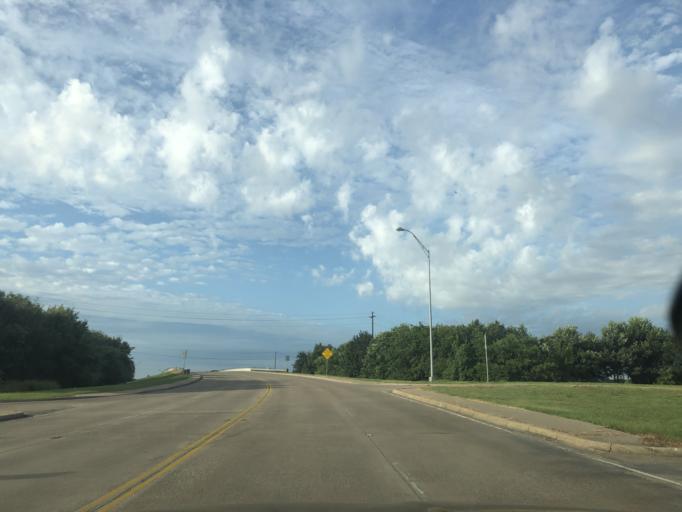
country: US
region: Texas
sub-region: Dallas County
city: Sunnyvale
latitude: 32.8473
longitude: -96.5828
